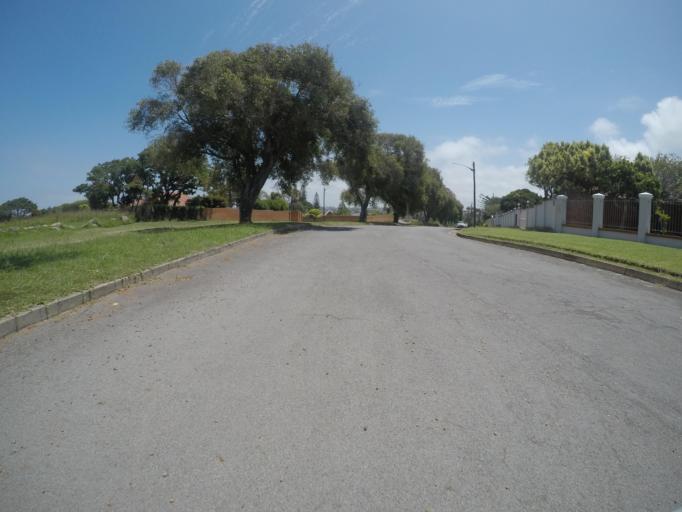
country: ZA
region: Eastern Cape
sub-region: Buffalo City Metropolitan Municipality
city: East London
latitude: -32.9979
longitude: 27.9268
